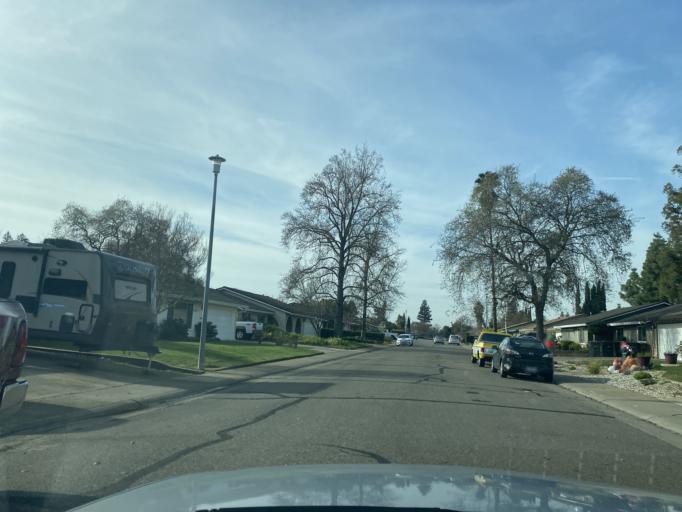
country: US
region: California
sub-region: Sacramento County
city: Elk Grove
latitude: 38.4025
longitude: -121.3784
